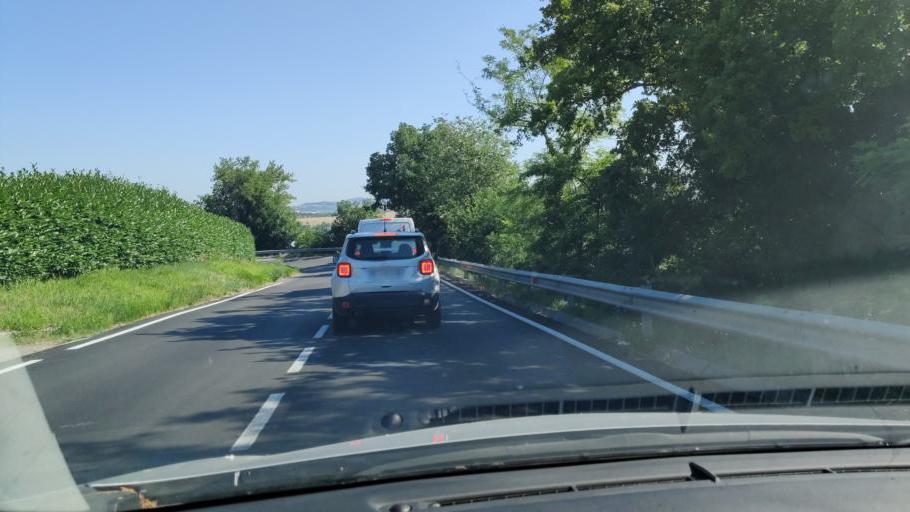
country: IT
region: Umbria
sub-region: Provincia di Perugia
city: Todi
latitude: 42.7843
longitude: 12.4187
